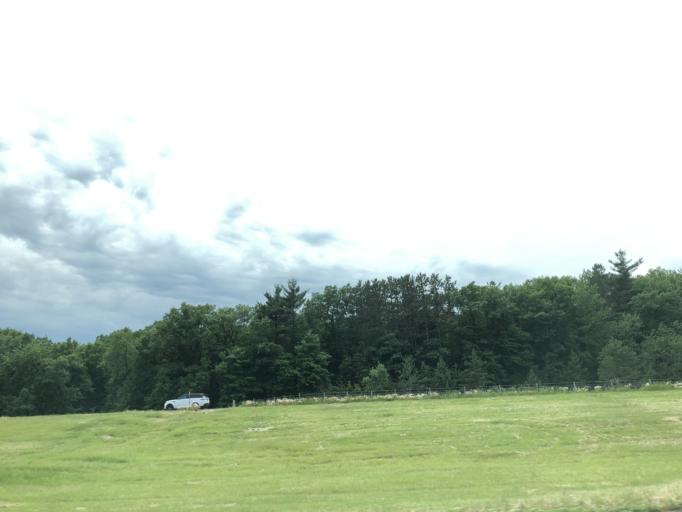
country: US
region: Minnesota
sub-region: Stearns County
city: Collegeville
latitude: 45.5887
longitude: -94.3675
